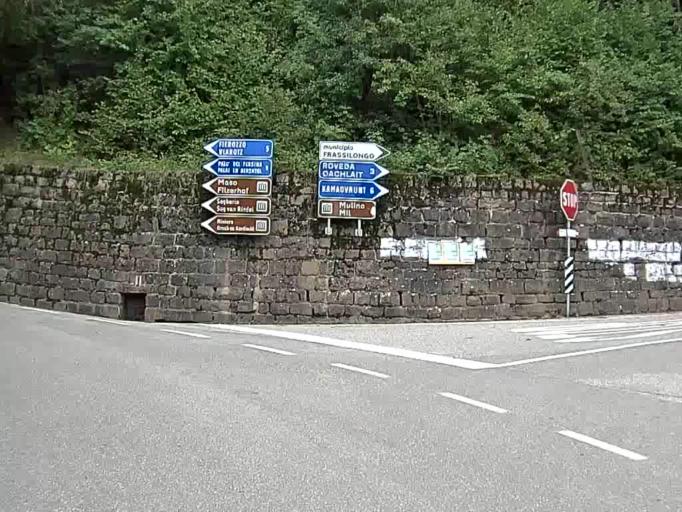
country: IT
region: Trentino-Alto Adige
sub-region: Provincia di Trento
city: Frassilongo
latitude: 46.0864
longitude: 11.2935
